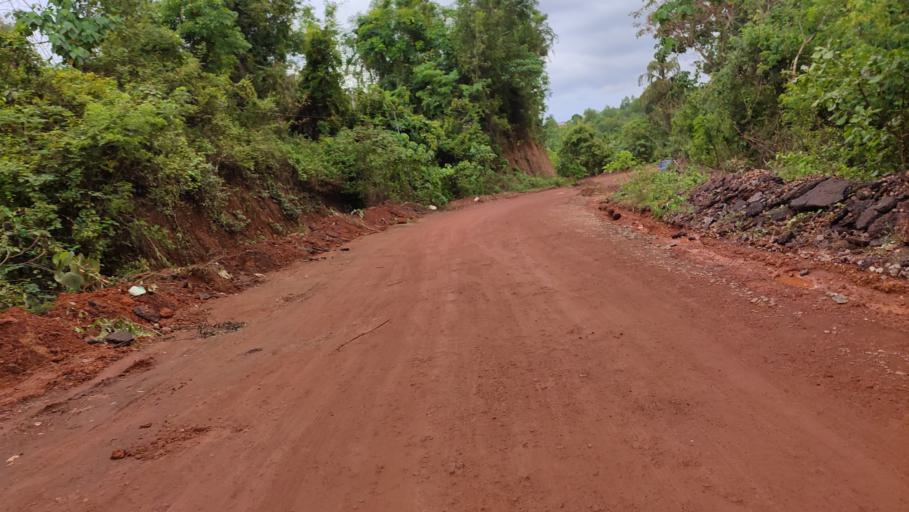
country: IN
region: Kerala
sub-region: Kasaragod District
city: Kasaragod
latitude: 12.5309
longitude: 75.0712
